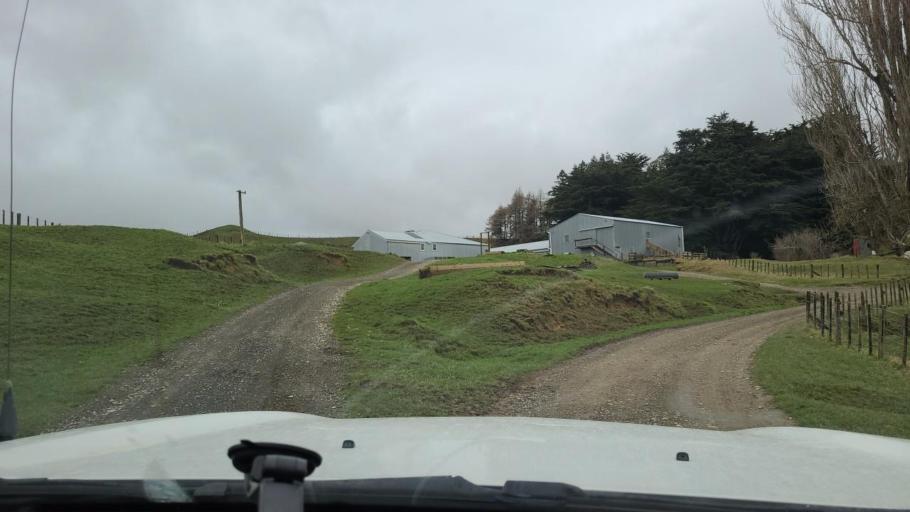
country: NZ
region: Hawke's Bay
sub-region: Wairoa District
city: Wairoa
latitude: -38.5669
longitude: 177.4769
